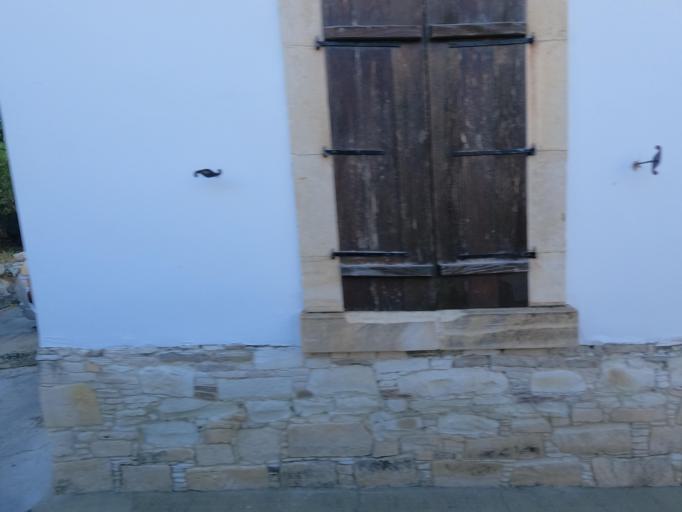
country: CY
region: Lefkosia
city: Alampra
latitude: 34.9886
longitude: 33.3984
